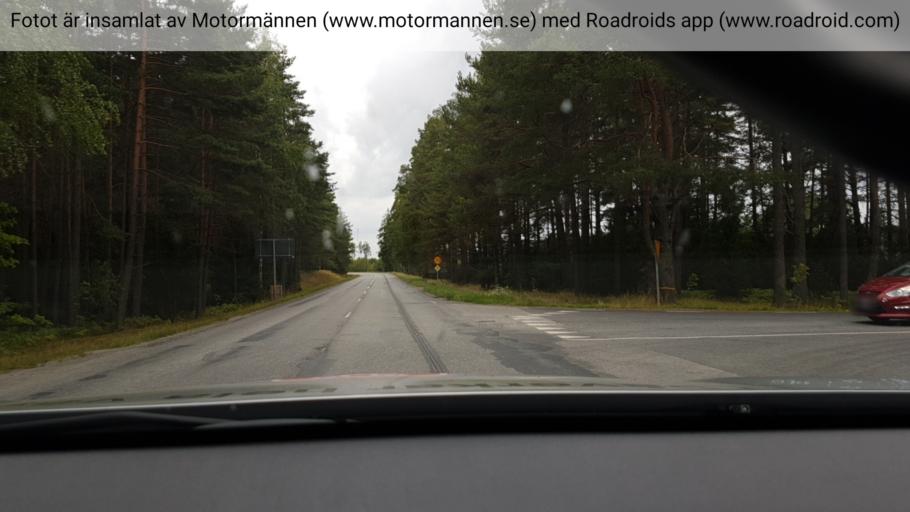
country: SE
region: Stockholm
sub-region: Sigtuna Kommun
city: Rosersberg
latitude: 59.6207
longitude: 17.9274
